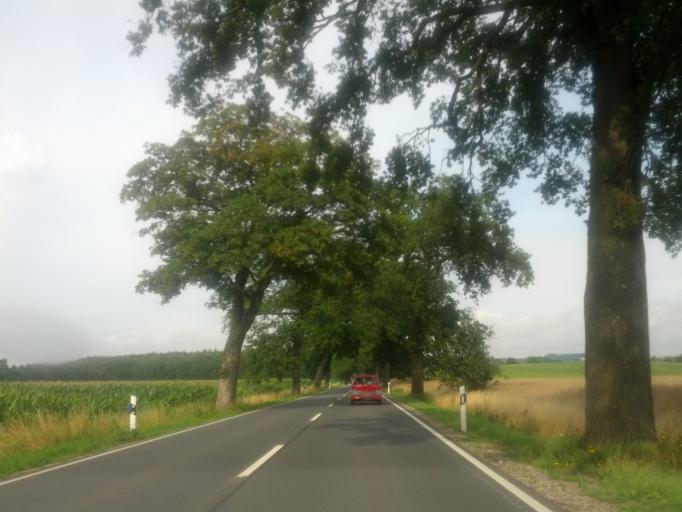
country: DE
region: Mecklenburg-Vorpommern
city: Sellin
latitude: 53.9170
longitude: 11.5867
